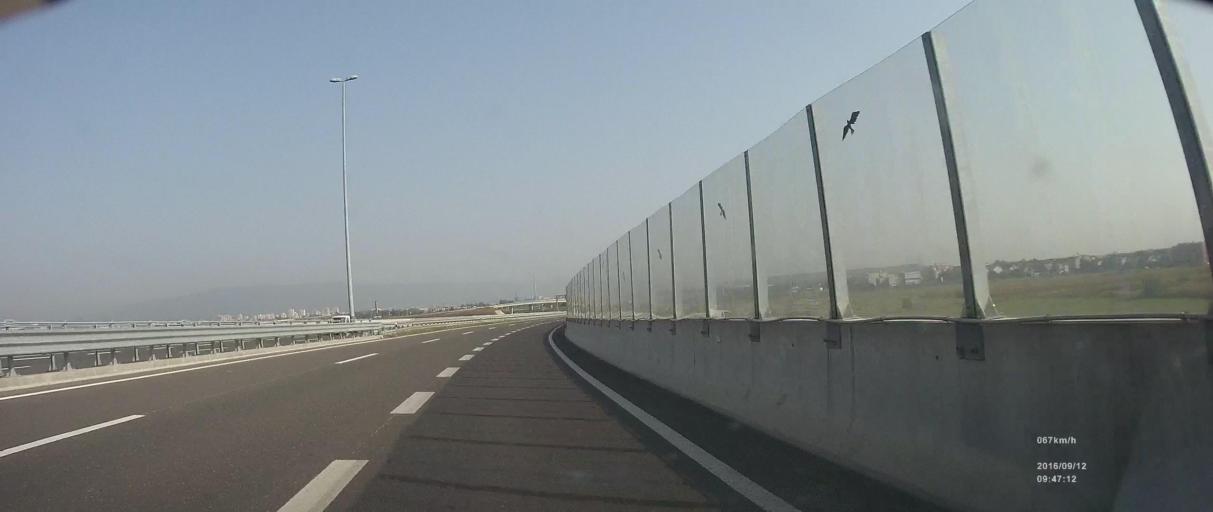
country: HR
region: Grad Zagreb
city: Odra
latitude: 45.7374
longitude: 16.0099
